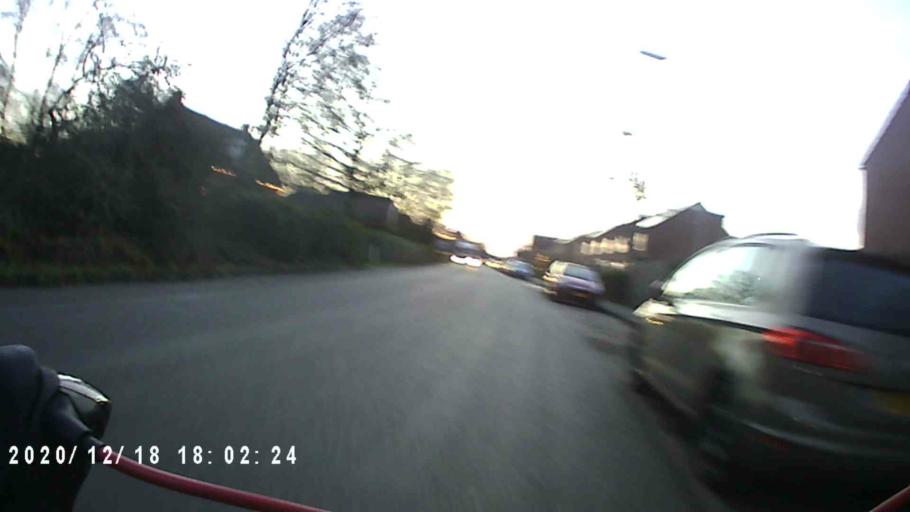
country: NL
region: Groningen
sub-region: Gemeente Haren
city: Haren
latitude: 53.1335
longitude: 6.5721
